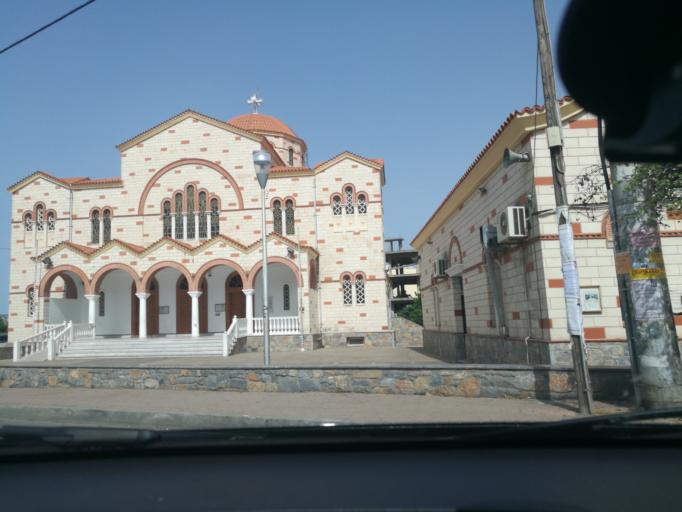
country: GR
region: Crete
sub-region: Nomos Irakleiou
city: Irakleion
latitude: 35.3249
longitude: 25.1298
